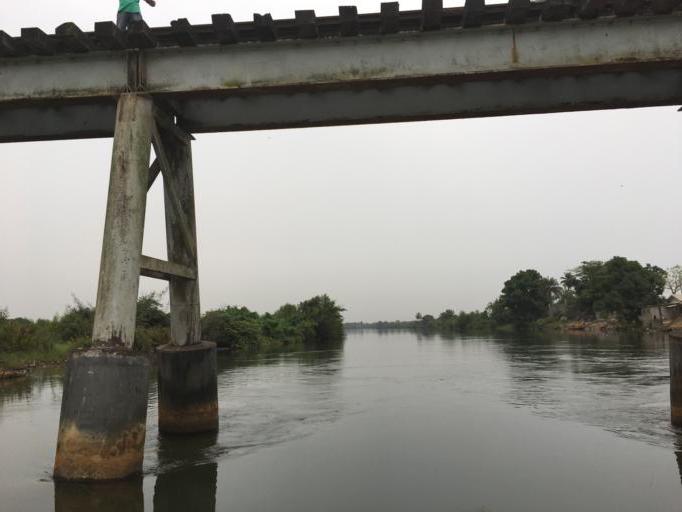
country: LR
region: Montserrado
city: Monrovia
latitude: 6.3713
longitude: -10.7786
